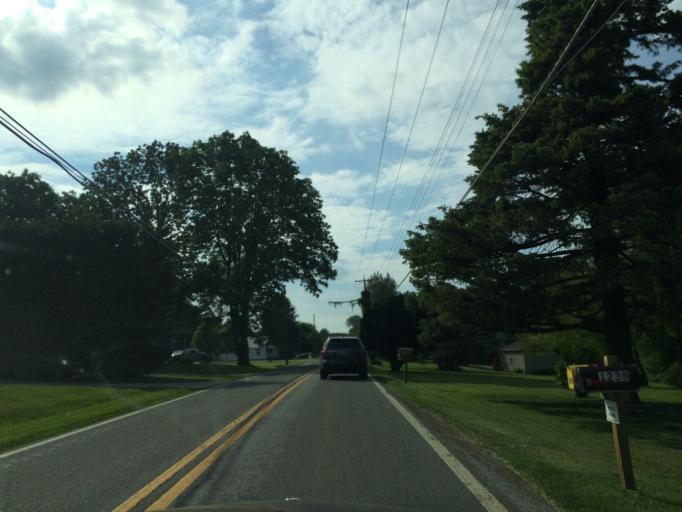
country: US
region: Maryland
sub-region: Carroll County
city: Westminster
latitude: 39.5083
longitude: -76.9502
